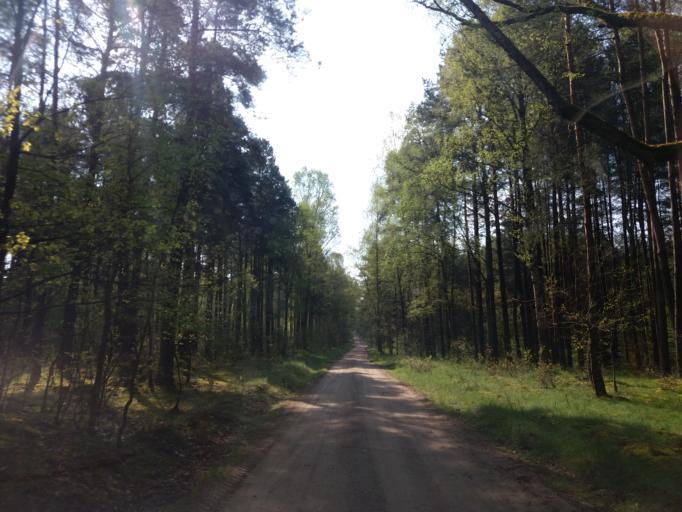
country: PL
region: West Pomeranian Voivodeship
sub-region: Powiat choszczenski
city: Drawno
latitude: 53.2162
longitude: 15.8288
